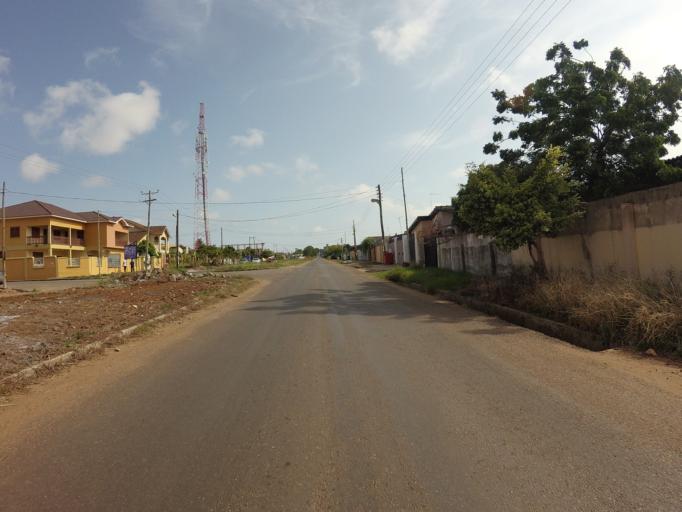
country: GH
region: Greater Accra
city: Nungua
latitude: 5.6416
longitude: -0.1007
